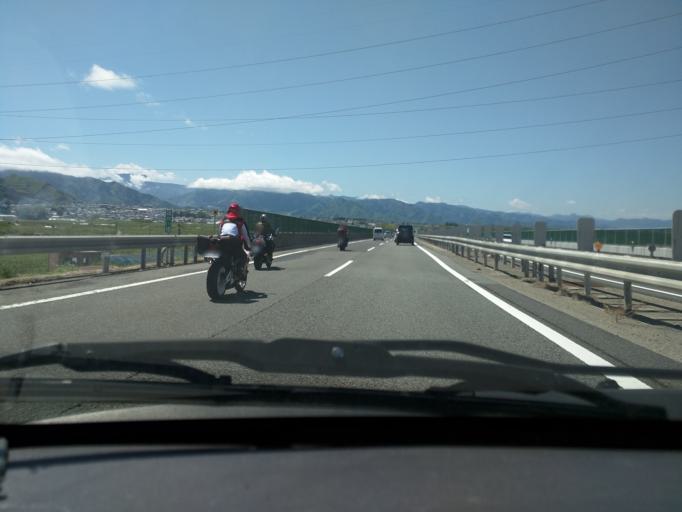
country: JP
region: Nagano
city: Nakano
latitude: 36.7255
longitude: 138.3160
